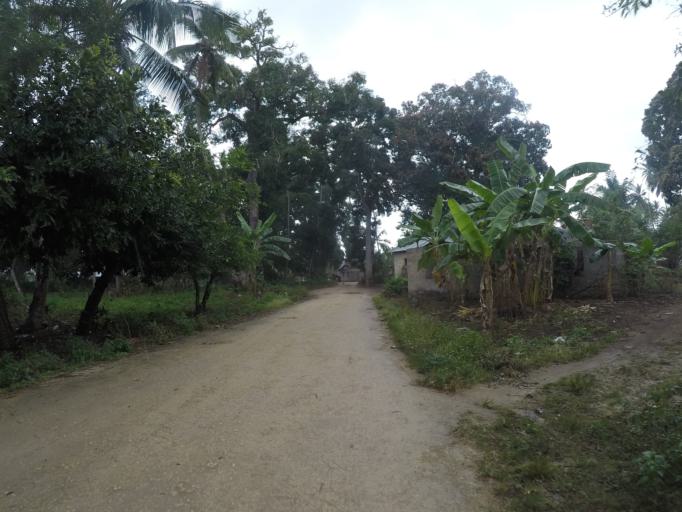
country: TZ
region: Zanzibar North
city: Mkokotoni
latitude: -5.9543
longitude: 39.1941
